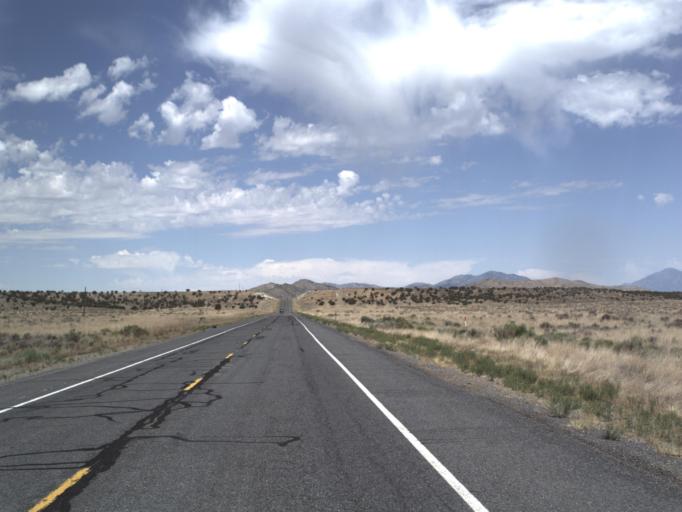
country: US
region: Utah
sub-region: Utah County
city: Eagle Mountain
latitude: 40.0608
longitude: -112.3127
